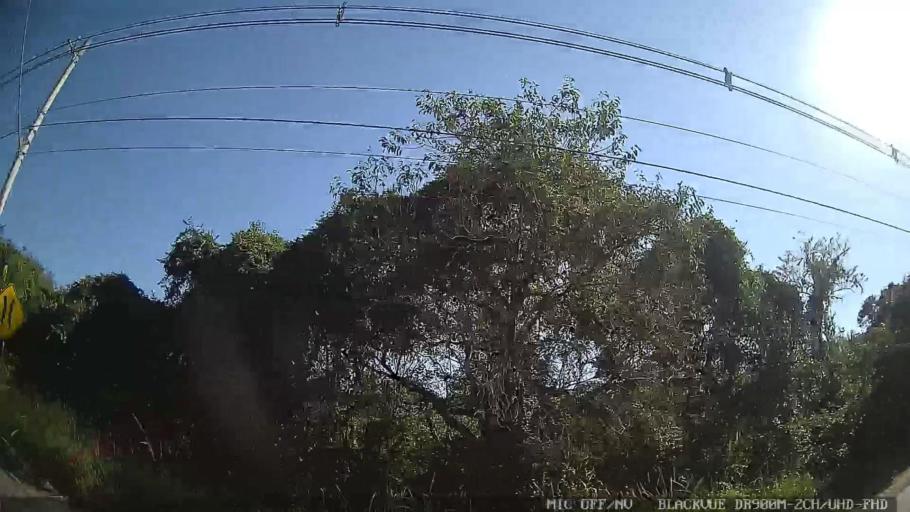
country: BR
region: Sao Paulo
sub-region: Santos
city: Santos
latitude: -23.9065
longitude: -46.3115
